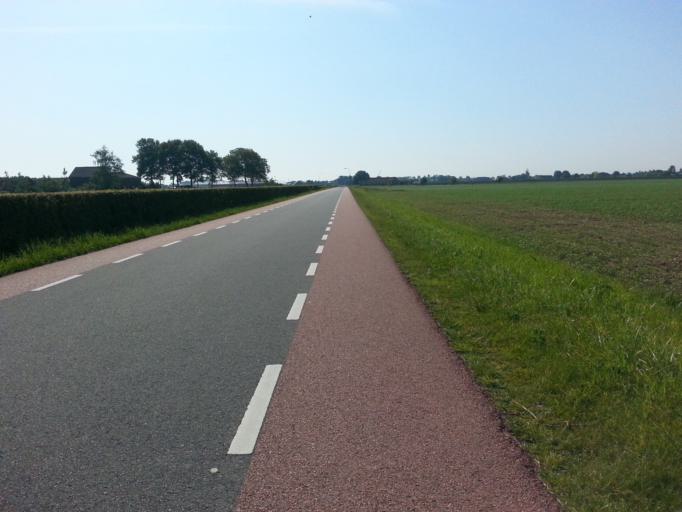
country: NL
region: Utrecht
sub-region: Gemeente Utrechtse Heuvelrug
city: Driebergen-Rijsenburg
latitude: 52.0055
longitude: 5.2915
